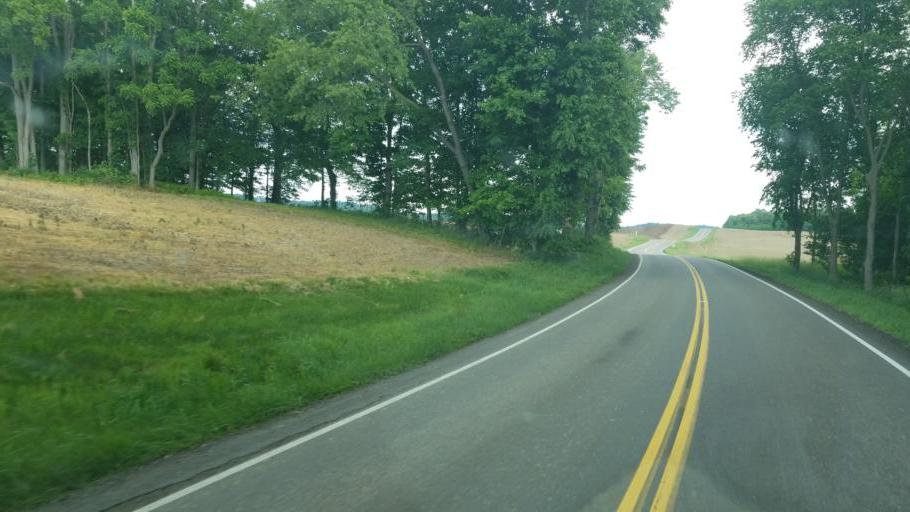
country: US
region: Ohio
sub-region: Knox County
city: Danville
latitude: 40.4818
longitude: -82.2774
